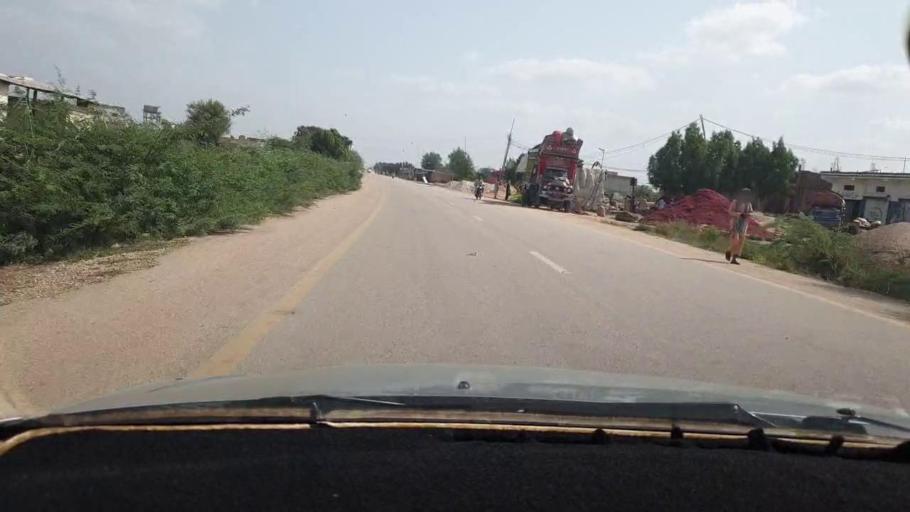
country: PK
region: Sindh
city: Naukot
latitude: 24.9770
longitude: 69.2948
